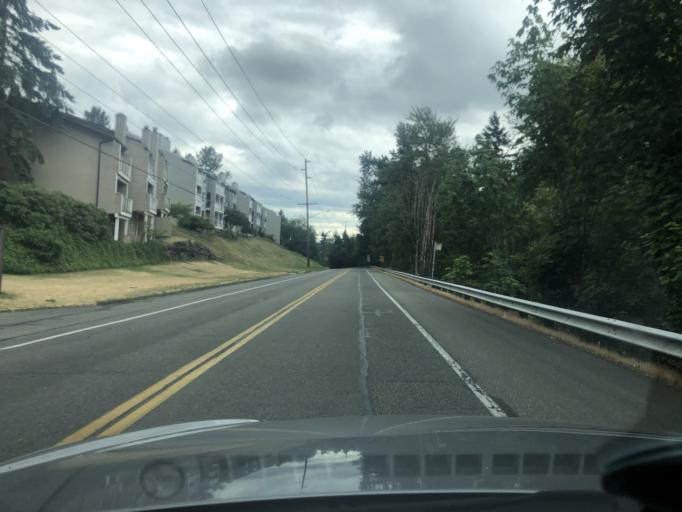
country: US
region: Washington
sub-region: King County
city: Lea Hill
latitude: 47.3203
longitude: -122.2011
